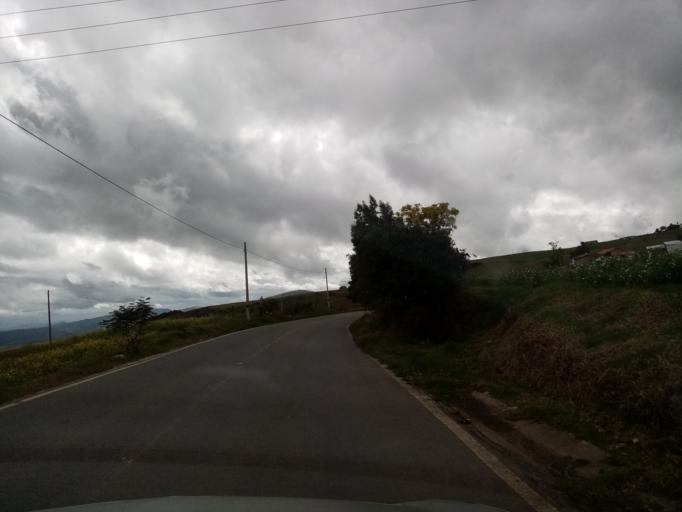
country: CO
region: Boyaca
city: Siachoque
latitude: 5.5654
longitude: -73.2797
